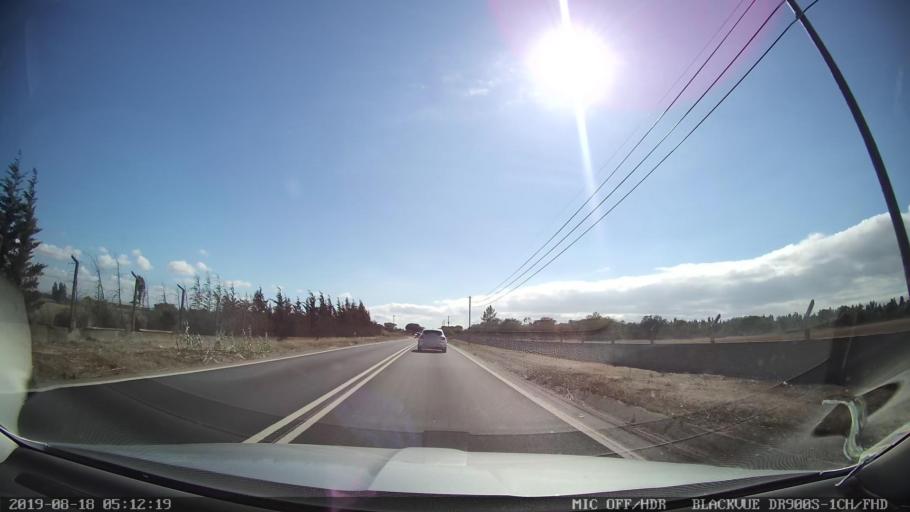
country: PT
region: Setubal
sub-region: Alcochete
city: Alcochete
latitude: 38.7695
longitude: -8.8971
